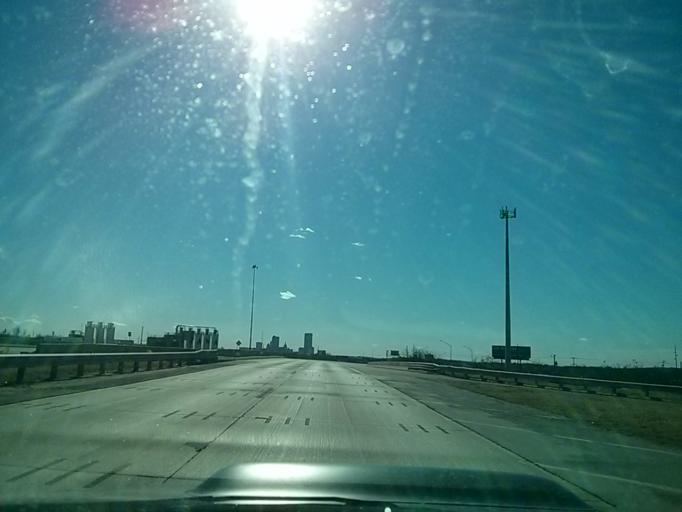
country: US
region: Oklahoma
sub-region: Tulsa County
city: Tulsa
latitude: 36.1915
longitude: -95.9556
